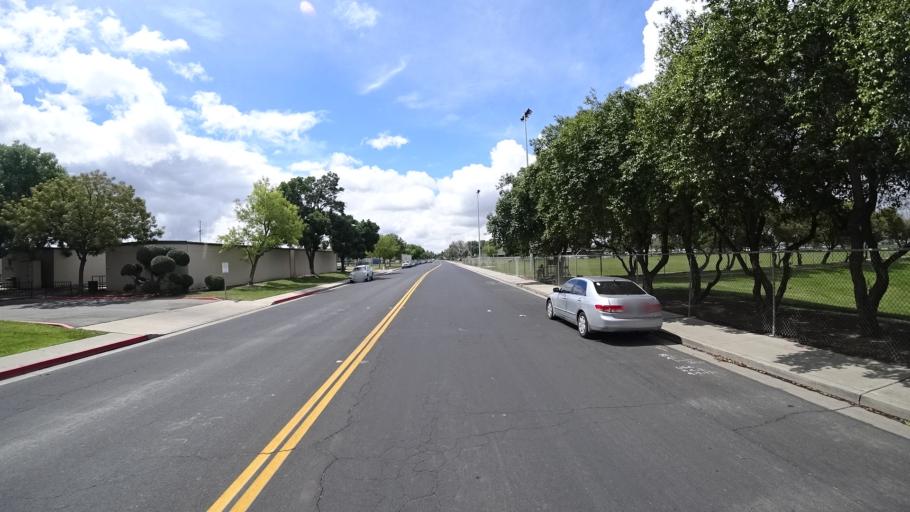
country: US
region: California
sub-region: Kings County
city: Hanford
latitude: 36.3339
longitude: -119.6633
